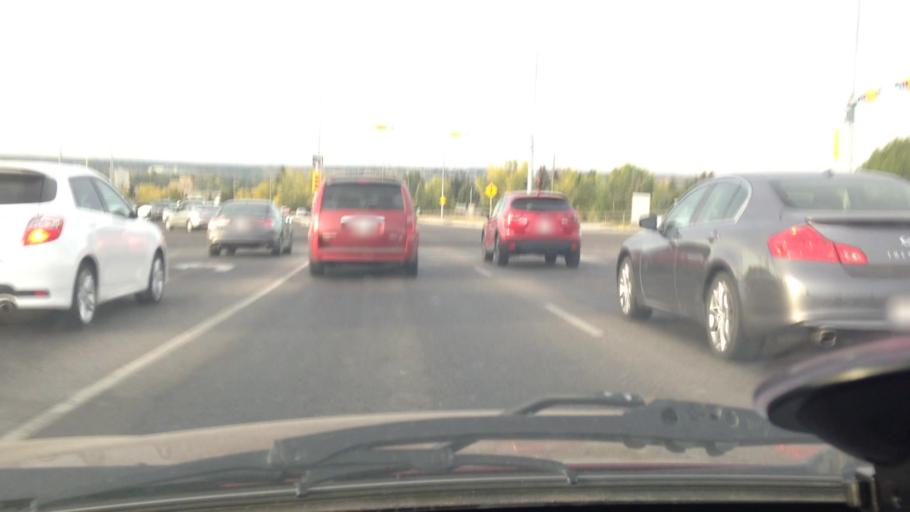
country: CA
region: Alberta
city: Calgary
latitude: 51.1095
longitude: -114.1399
